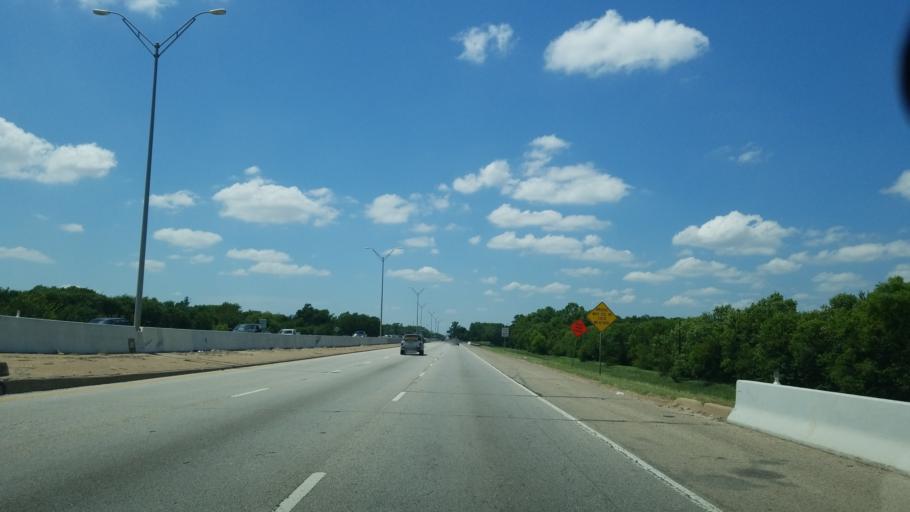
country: US
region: Texas
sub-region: Dallas County
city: Hutchins
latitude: 32.7400
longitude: -96.7197
